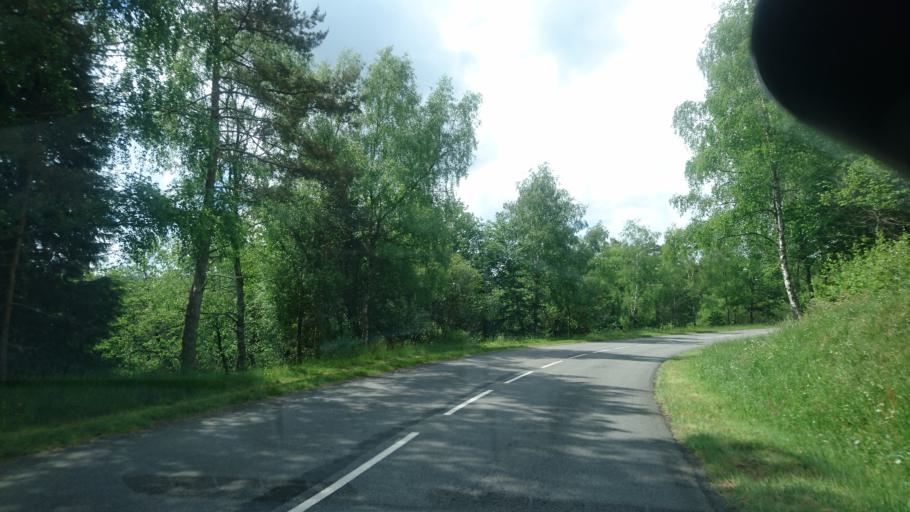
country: FR
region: Limousin
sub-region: Departement de la Haute-Vienne
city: Peyrat-le-Chateau
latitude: 45.7795
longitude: 1.8657
